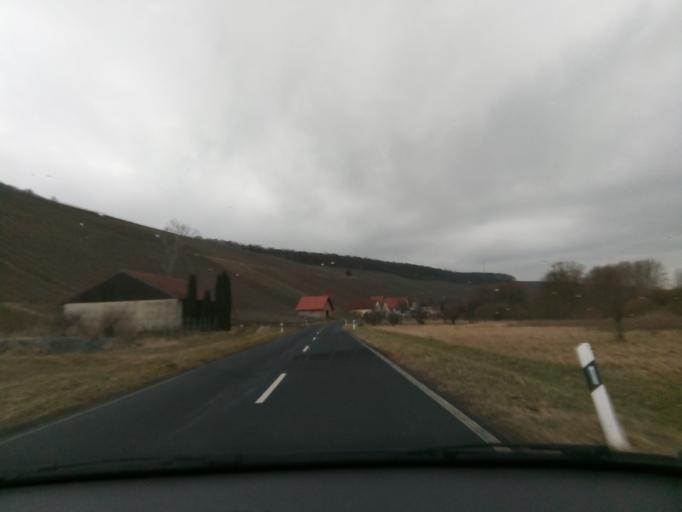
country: DE
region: Bavaria
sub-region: Regierungsbezirk Unterfranken
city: Nordheim
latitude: 49.8439
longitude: 10.1703
